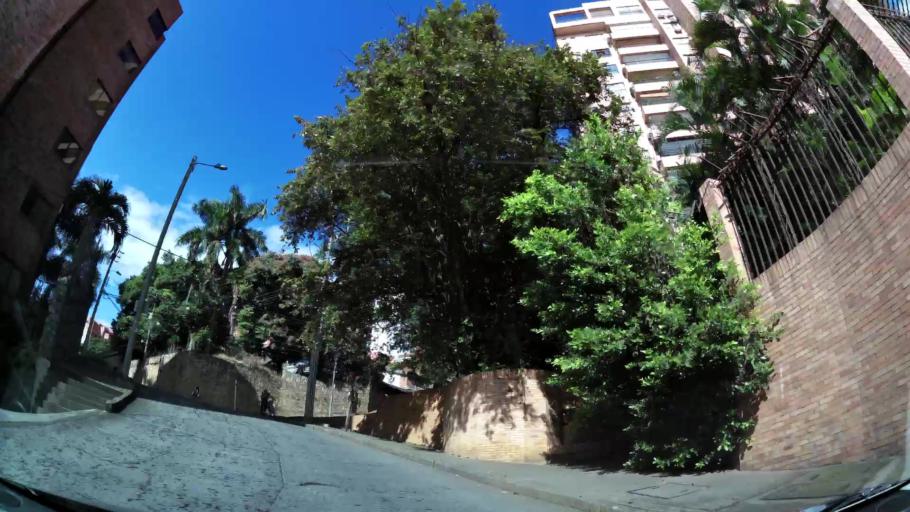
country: CO
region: Valle del Cauca
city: Cali
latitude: 3.4587
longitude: -76.5370
